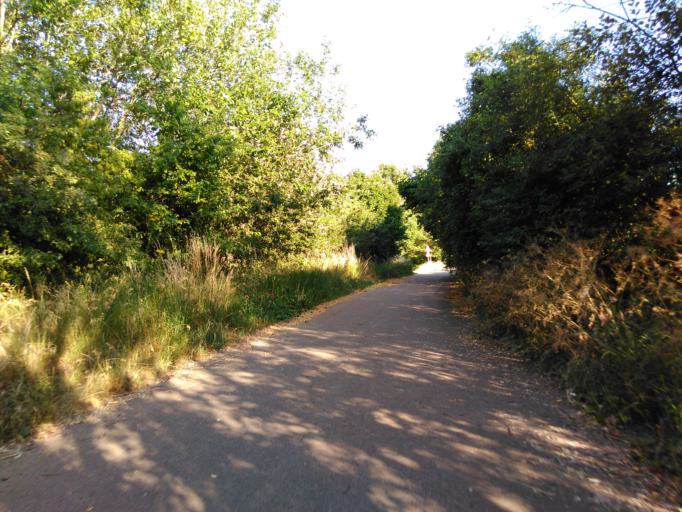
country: LU
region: Luxembourg
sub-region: Canton d'Esch-sur-Alzette
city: Petange
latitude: 49.5603
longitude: 5.8852
